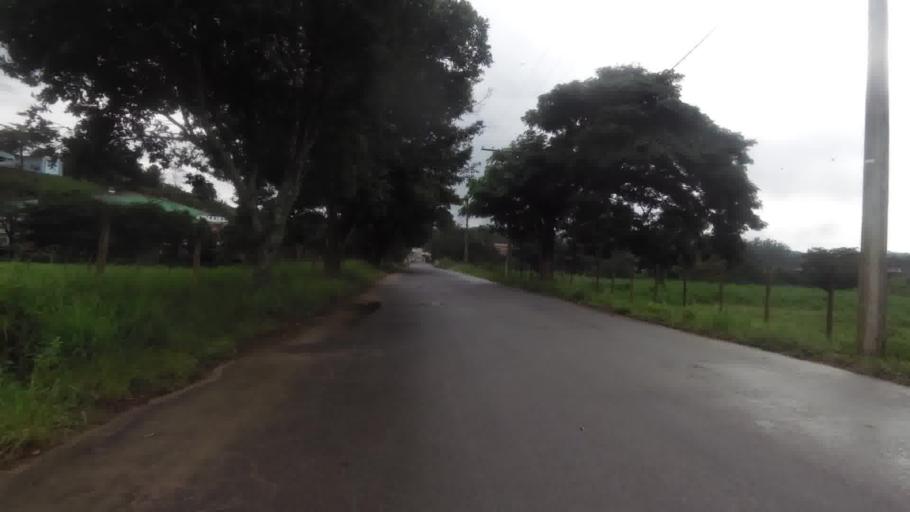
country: BR
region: Espirito Santo
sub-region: Alfredo Chaves
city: Alfredo Chaves
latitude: -20.6875
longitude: -40.6796
